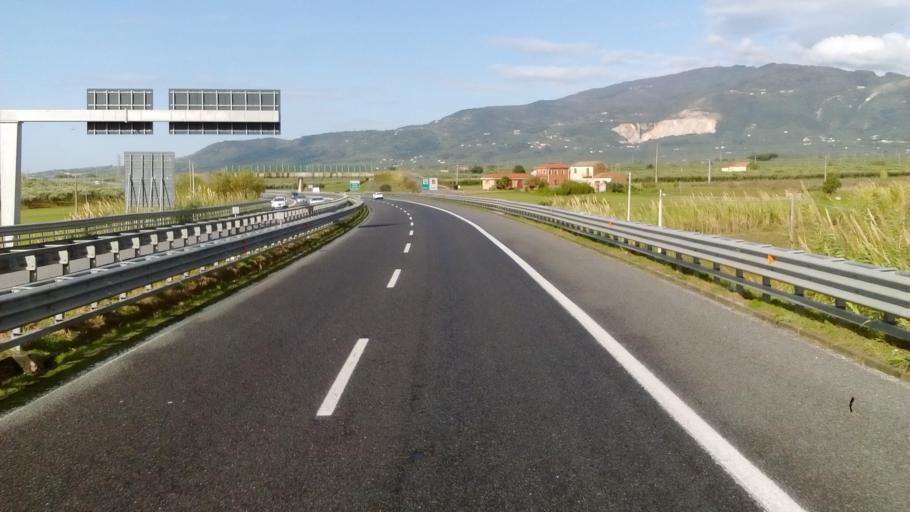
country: IT
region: Calabria
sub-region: Provincia di Catanzaro
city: Santa Eufemia Lamezia
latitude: 38.9211
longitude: 16.2626
